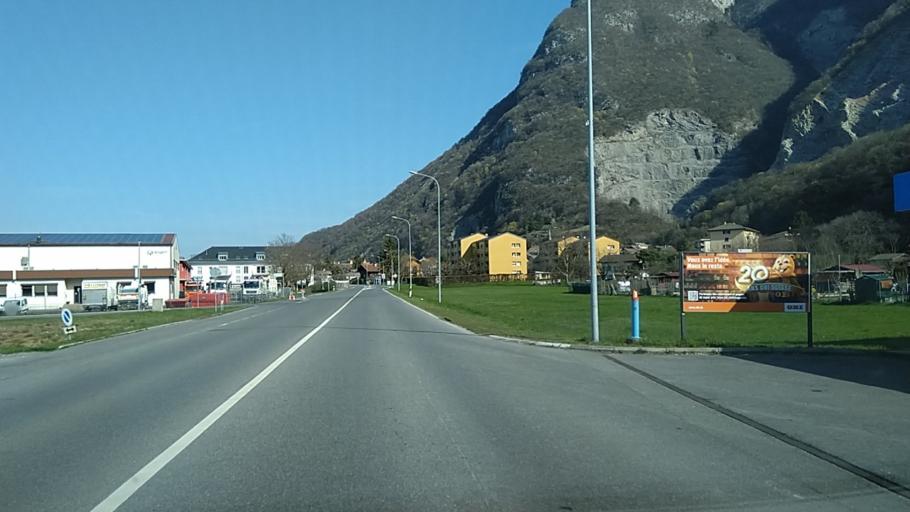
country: CH
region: Vaud
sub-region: Aigle District
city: Villeneuve
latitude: 46.3553
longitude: 6.9324
